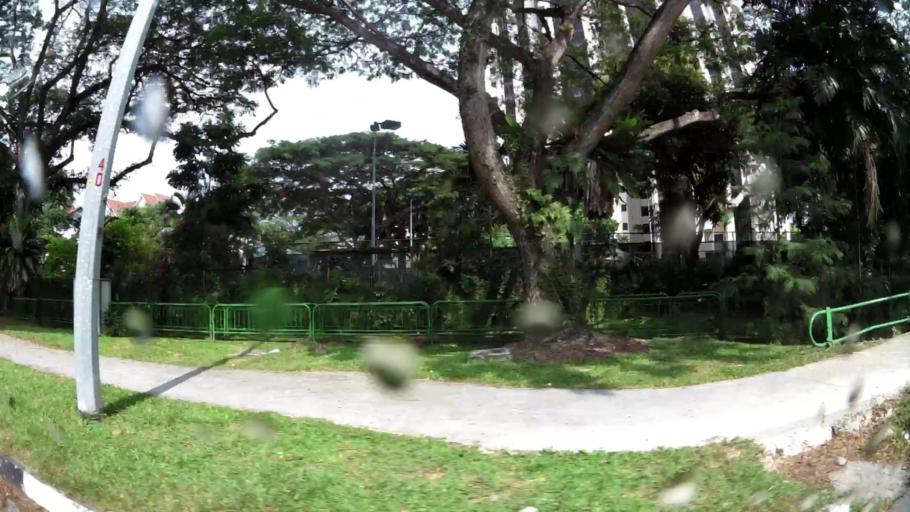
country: SG
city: Singapore
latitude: 1.3114
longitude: 103.9345
